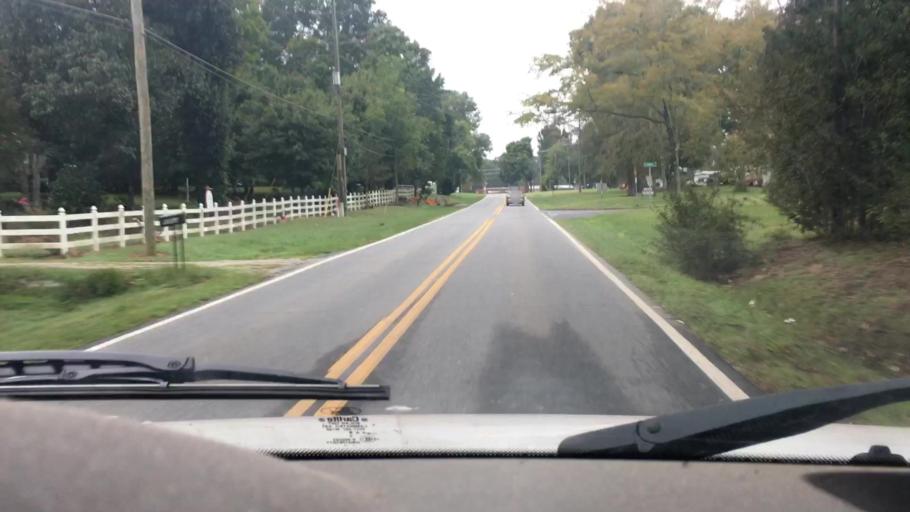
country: US
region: North Carolina
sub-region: Lincoln County
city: Denver
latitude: 35.5349
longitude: -81.0286
